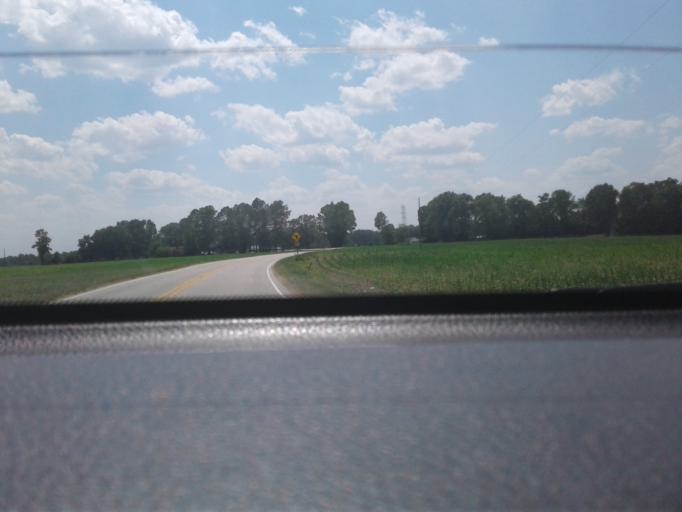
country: US
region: North Carolina
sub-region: Harnett County
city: Erwin
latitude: 35.2905
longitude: -78.6679
